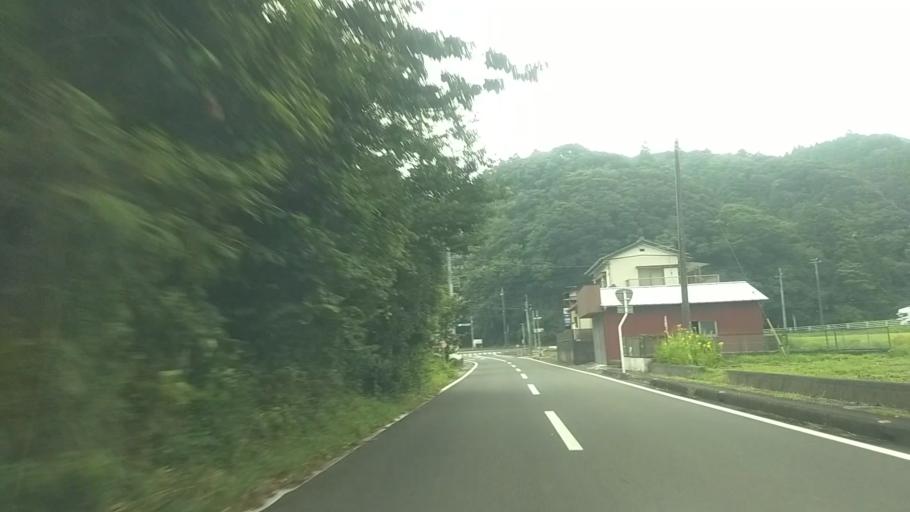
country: JP
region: Chiba
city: Ohara
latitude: 35.2698
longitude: 140.2545
